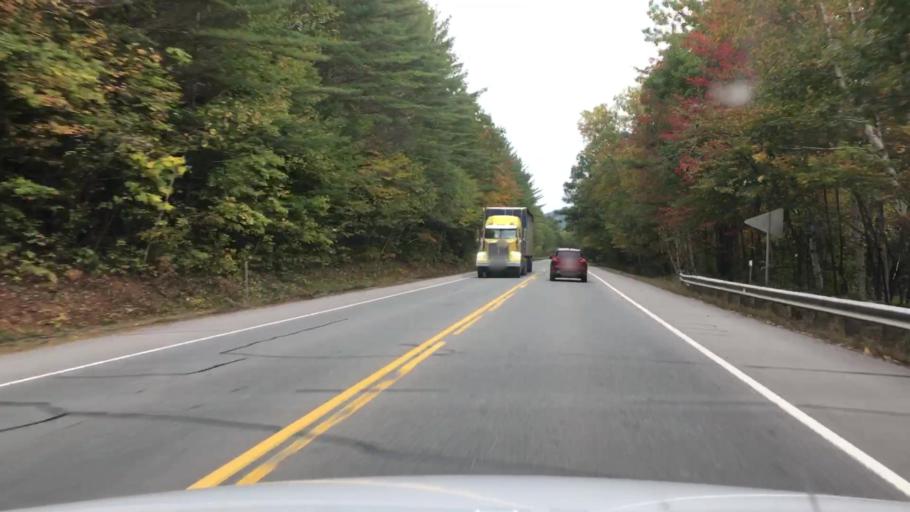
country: US
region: New Hampshire
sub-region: Coos County
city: Gorham
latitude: 44.3864
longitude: -71.0256
